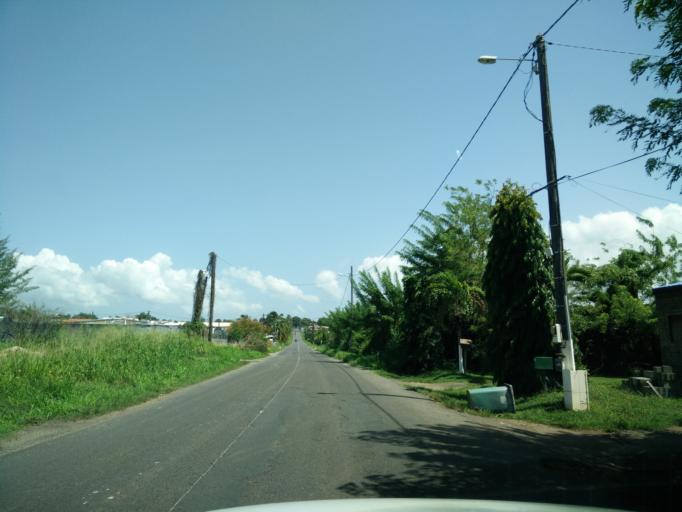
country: GP
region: Guadeloupe
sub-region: Guadeloupe
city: Petit-Bourg
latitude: 16.1769
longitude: -61.5869
